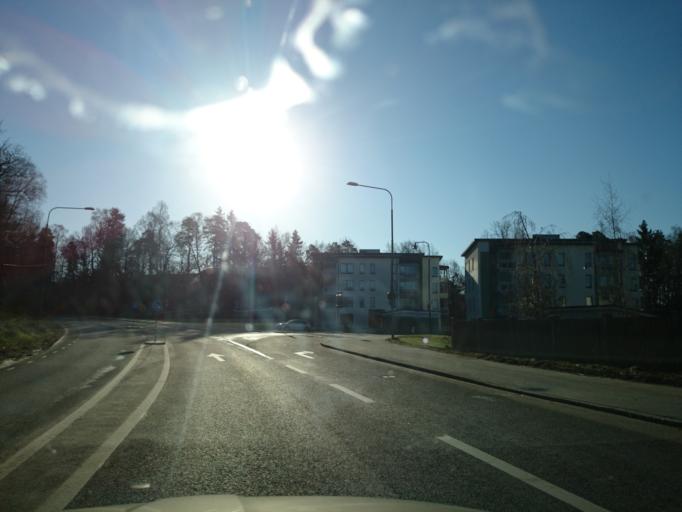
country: SE
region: Stockholm
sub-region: Stockholms Kommun
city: Arsta
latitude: 59.2514
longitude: 18.0518
